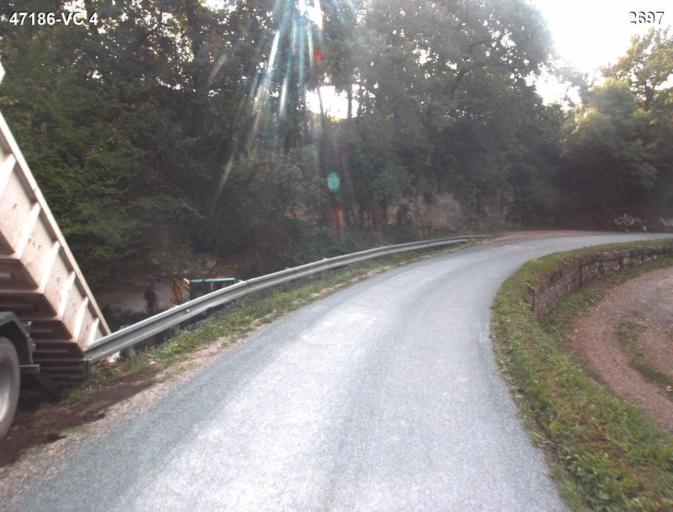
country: FR
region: Aquitaine
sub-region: Departement du Lot-et-Garonne
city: Port-Sainte-Marie
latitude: 44.2013
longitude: 0.4416
